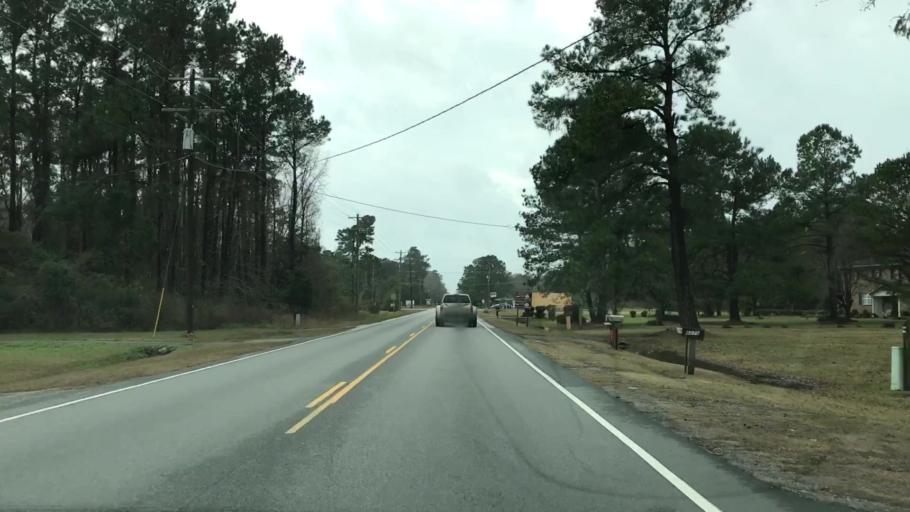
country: US
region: South Carolina
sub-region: Horry County
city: Socastee
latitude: 33.6925
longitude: -79.1163
